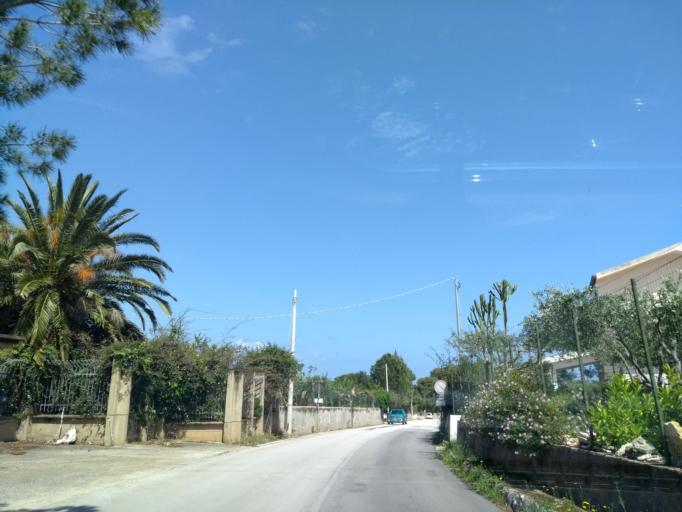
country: IT
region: Sicily
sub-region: Trapani
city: Castellammare del Golfo
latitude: 38.0517
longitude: 12.8407
